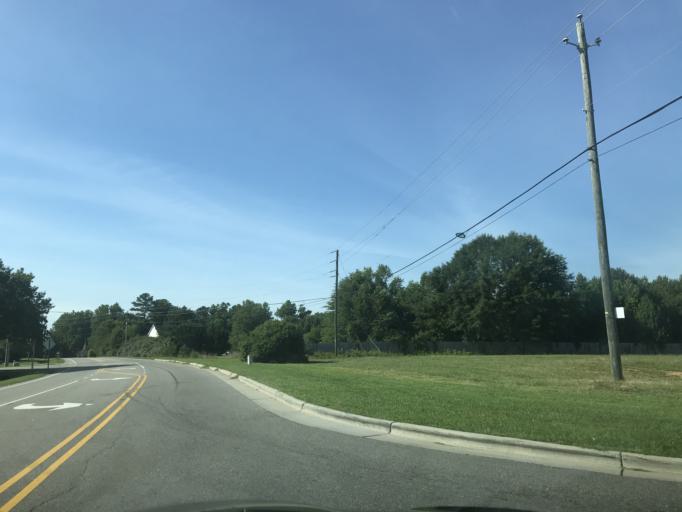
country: US
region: North Carolina
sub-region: Johnston County
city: Clayton
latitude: 35.6181
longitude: -78.5355
